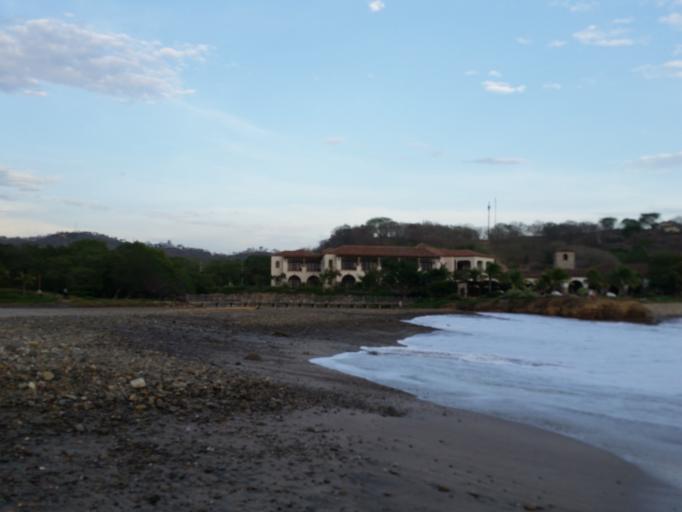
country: NI
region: Rivas
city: Tola
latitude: 11.4429
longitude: -86.0868
